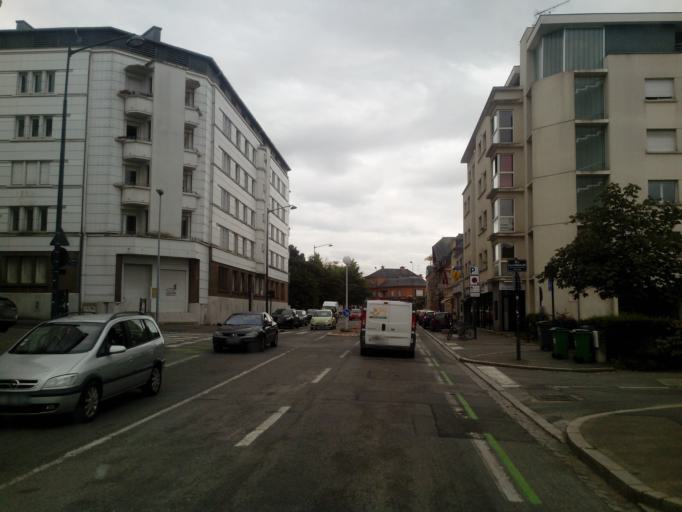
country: FR
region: Brittany
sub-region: Departement d'Ille-et-Vilaine
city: Rennes
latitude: 48.1054
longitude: -1.6506
